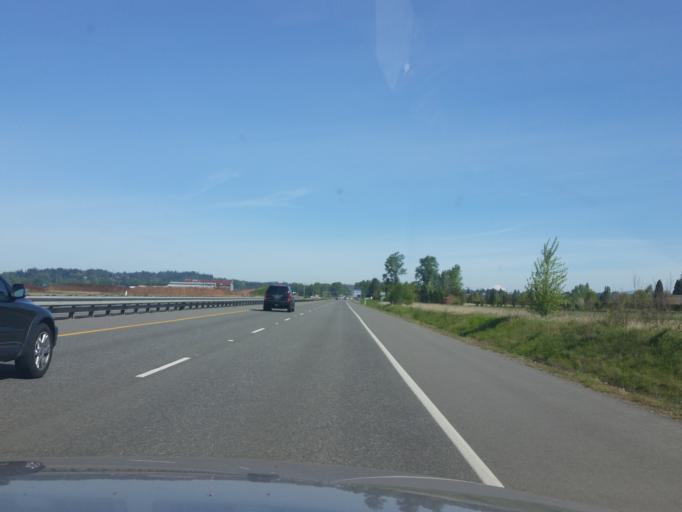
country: US
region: Washington
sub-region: Snohomish County
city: Snohomish
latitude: 47.8921
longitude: -122.1094
